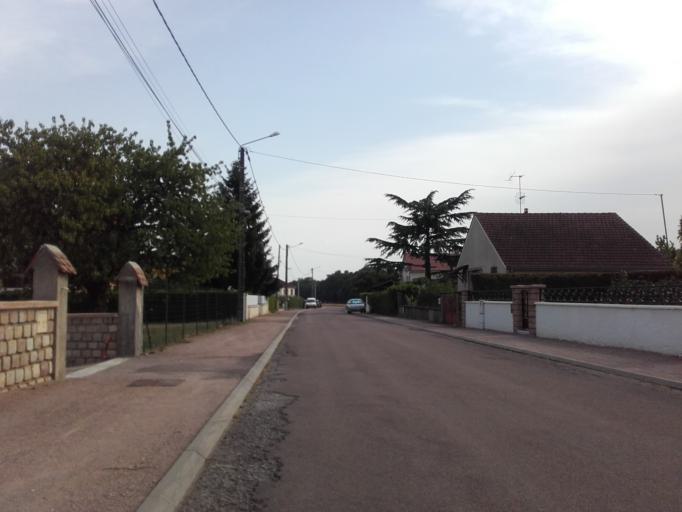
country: FR
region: Bourgogne
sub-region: Departement de Saone-et-Loire
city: Chagny
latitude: 46.8976
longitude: 4.7586
